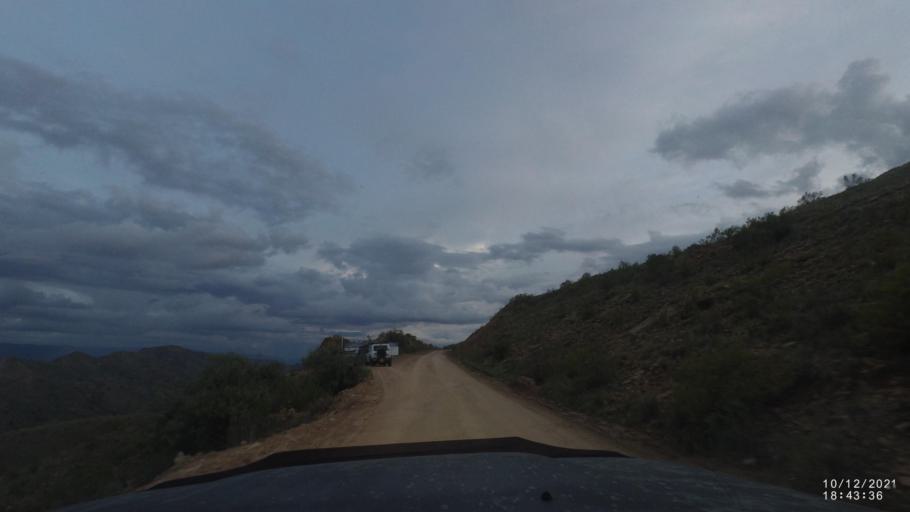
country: BO
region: Cochabamba
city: Tarata
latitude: -17.8767
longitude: -65.9783
